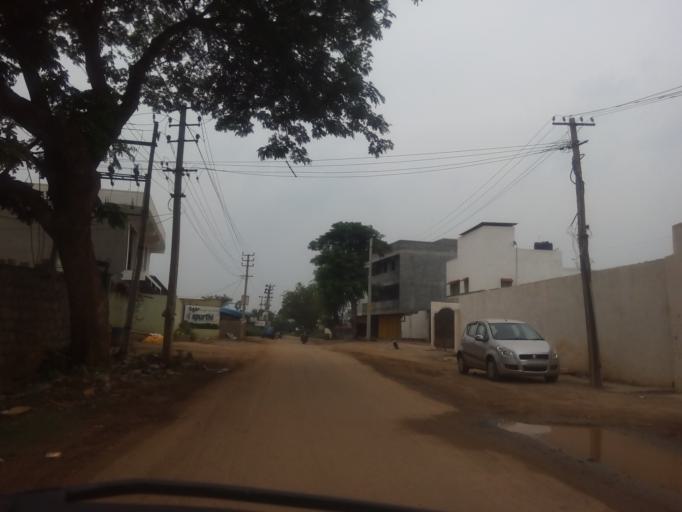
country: IN
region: Karnataka
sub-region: Bangalore Urban
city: Anekal
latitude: 12.8396
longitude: 77.6973
